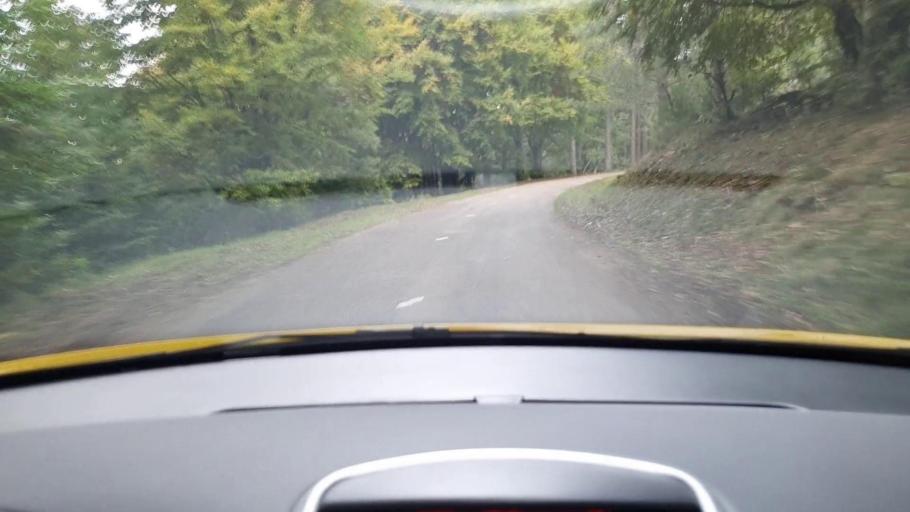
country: FR
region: Languedoc-Roussillon
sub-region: Departement de la Lozere
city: Meyrueis
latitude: 44.0901
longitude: 3.4559
